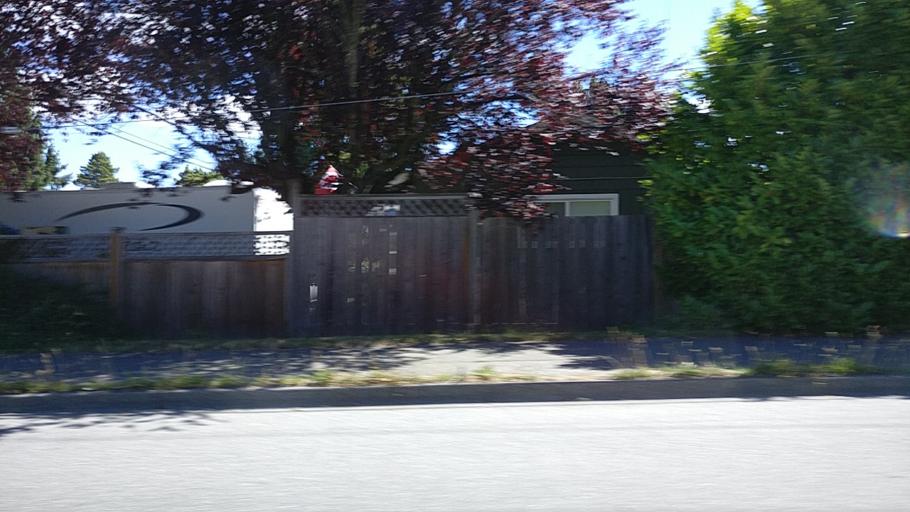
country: CA
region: British Columbia
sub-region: Greater Vancouver Regional District
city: White Rock
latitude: 49.0336
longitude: -122.7957
